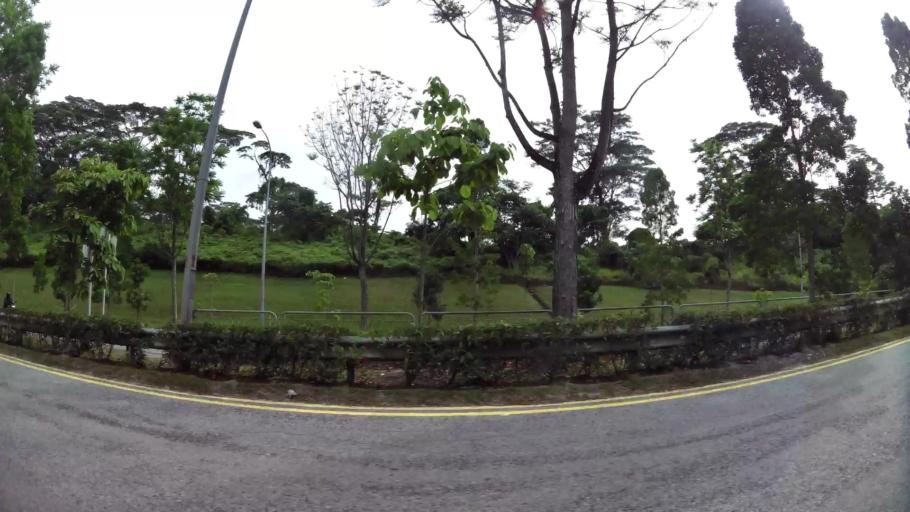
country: MY
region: Johor
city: Johor Bahru
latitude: 1.4162
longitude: 103.7639
